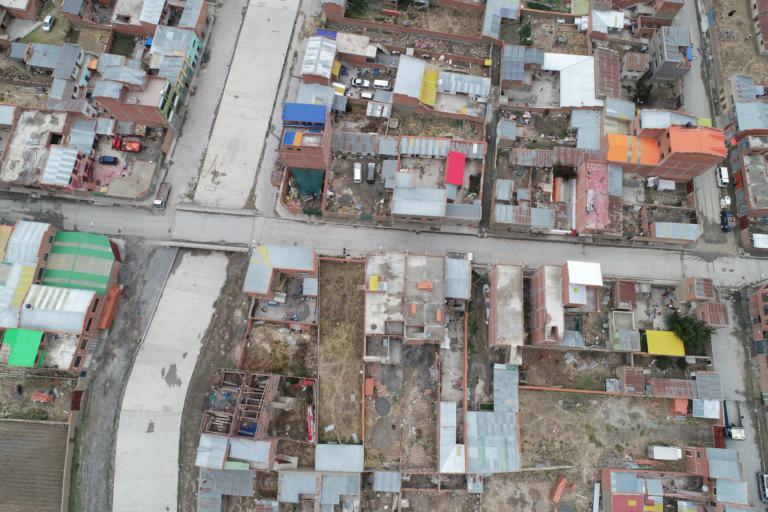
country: BO
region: La Paz
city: Achacachi
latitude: -16.0492
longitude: -68.6842
